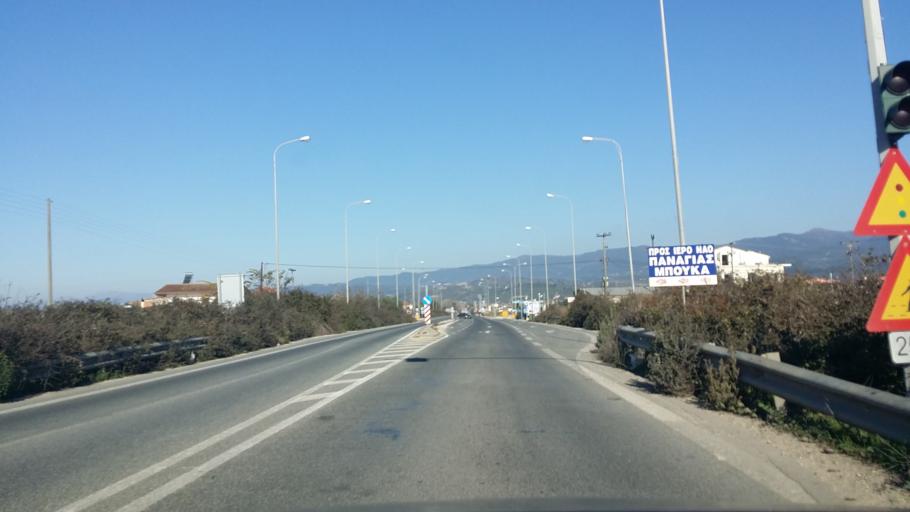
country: GR
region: West Greece
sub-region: Nomos Aitolias kai Akarnanias
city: Krikellos
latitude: 38.9286
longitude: 21.1774
